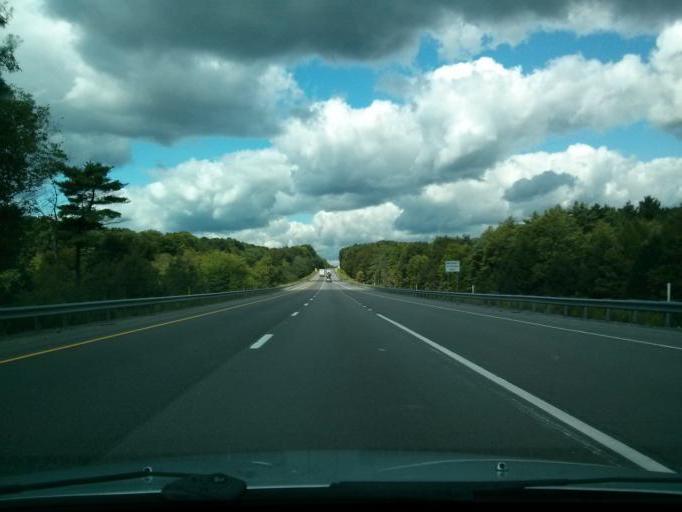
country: US
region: Pennsylvania
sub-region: Clearfield County
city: Treasure Lake
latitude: 41.1315
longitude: -78.7139
